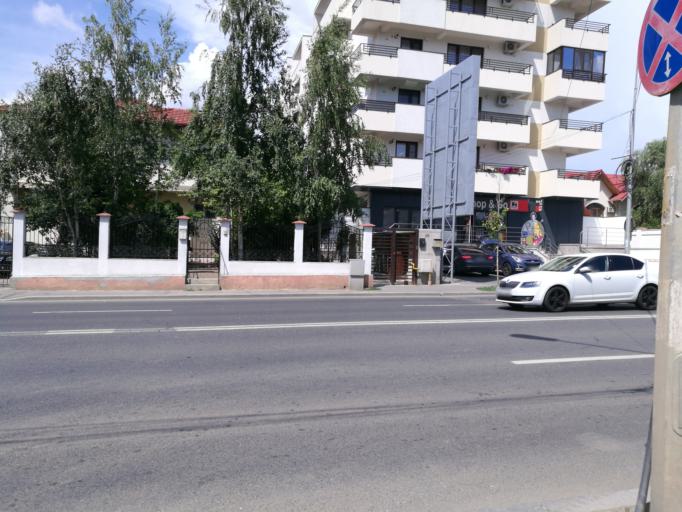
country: RO
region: Ilfov
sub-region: Comuna Otopeni
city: Otopeni
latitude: 44.5032
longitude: 26.0502
